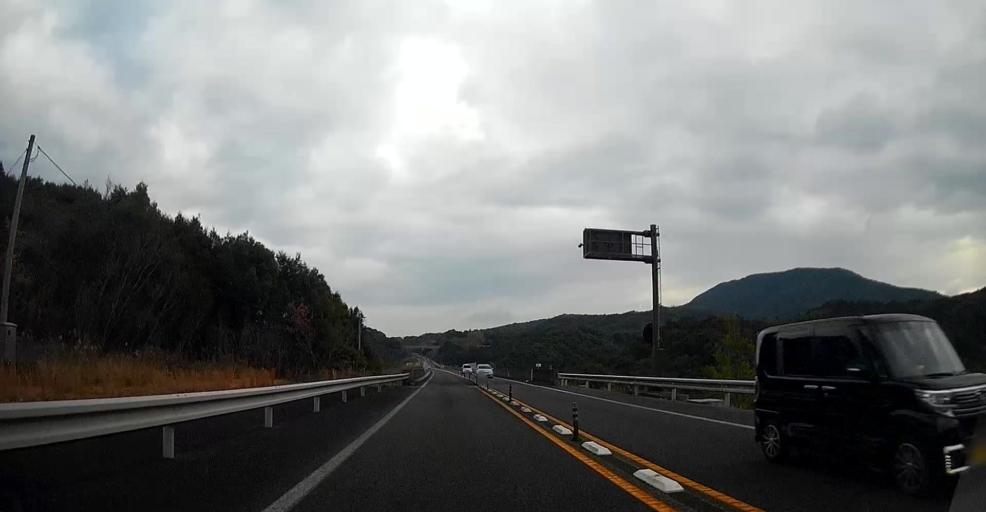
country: JP
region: Kumamoto
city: Hondo
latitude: 32.5080
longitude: 130.3388
